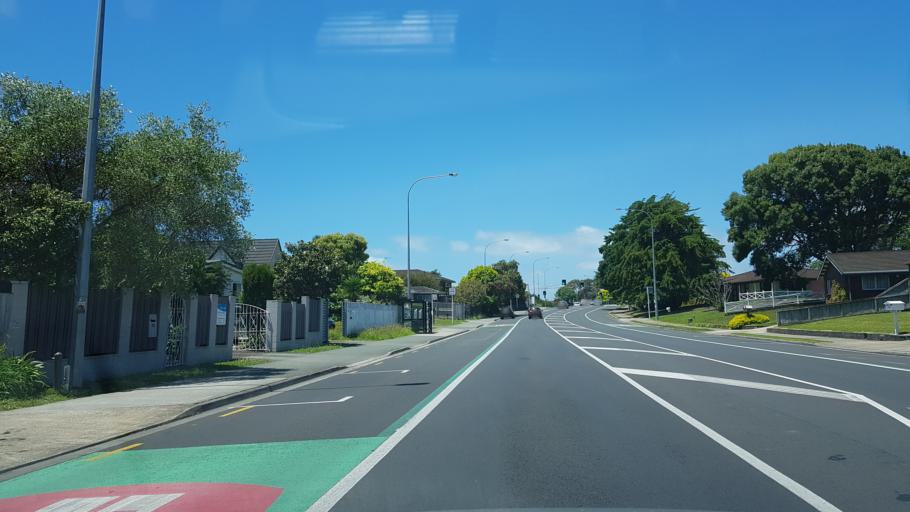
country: NZ
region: Auckland
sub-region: Auckland
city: North Shore
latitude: -36.7950
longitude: 174.7525
